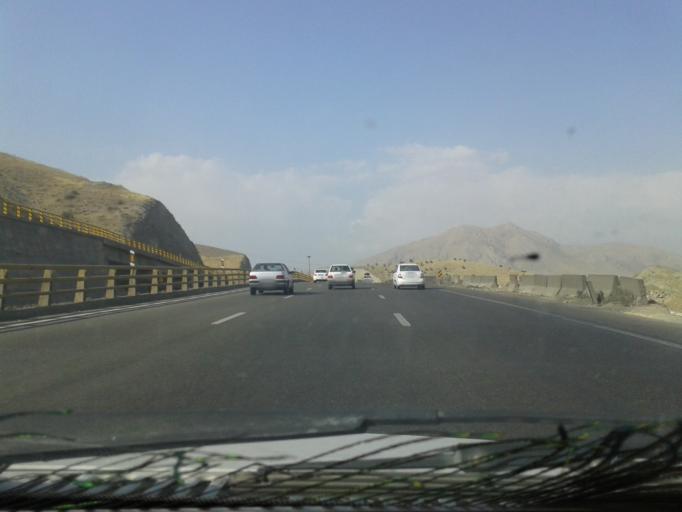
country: IR
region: Tehran
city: Pakdasht
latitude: 35.7332
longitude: 51.6783
